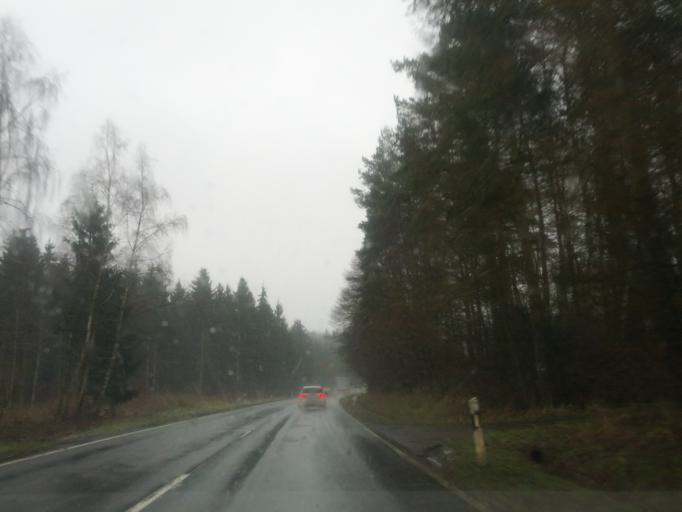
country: DE
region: Thuringia
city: Gerstungen
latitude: 51.0224
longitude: 10.0335
